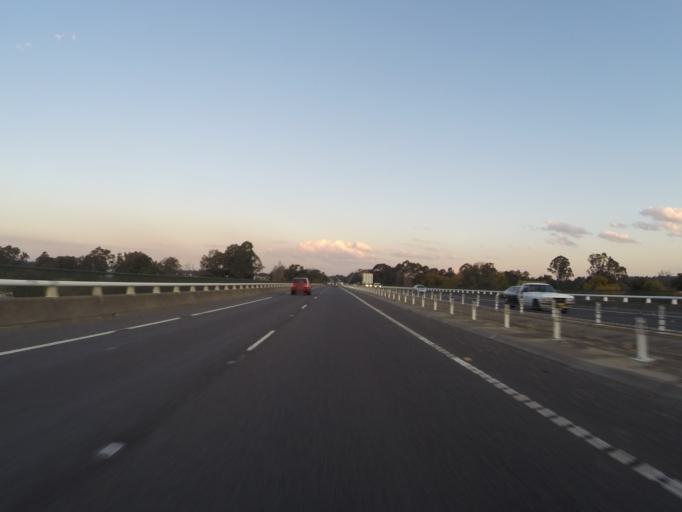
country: AU
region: New South Wales
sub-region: Penrith Municipality
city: Glenmore Park
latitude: -33.7635
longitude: 150.6586
